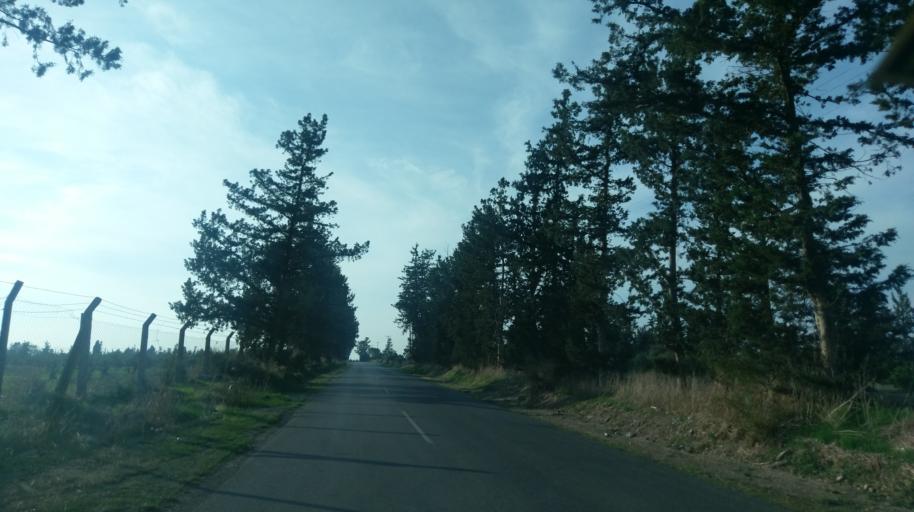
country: CY
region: Ammochostos
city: Achna
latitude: 35.1102
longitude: 33.7373
